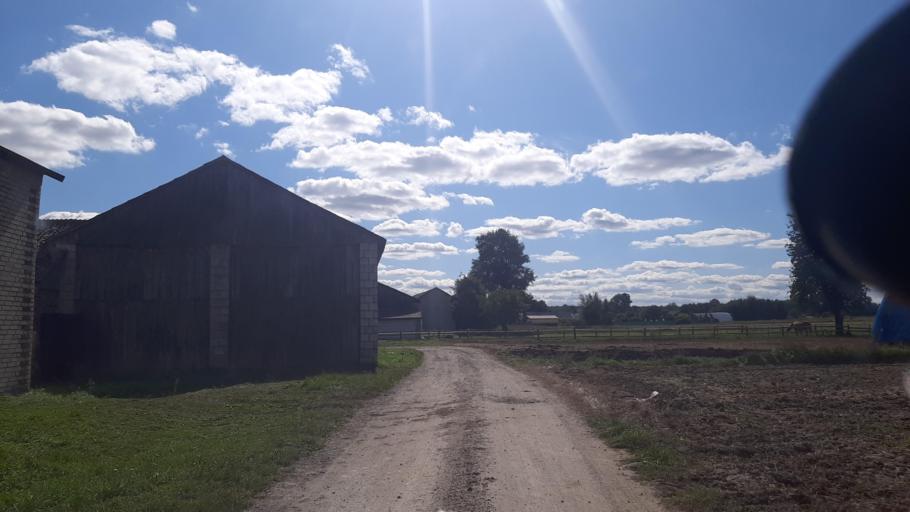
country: PL
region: Lublin Voivodeship
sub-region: Powiat lubartowski
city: Kamionka
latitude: 51.4077
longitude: 22.4153
